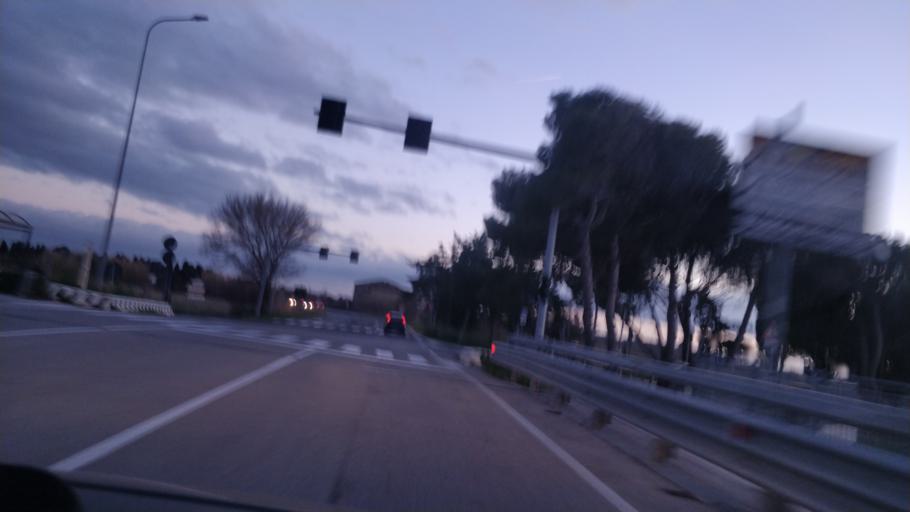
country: IT
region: Tuscany
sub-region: Provincia di Livorno
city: Vada
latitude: 43.3712
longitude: 10.4500
